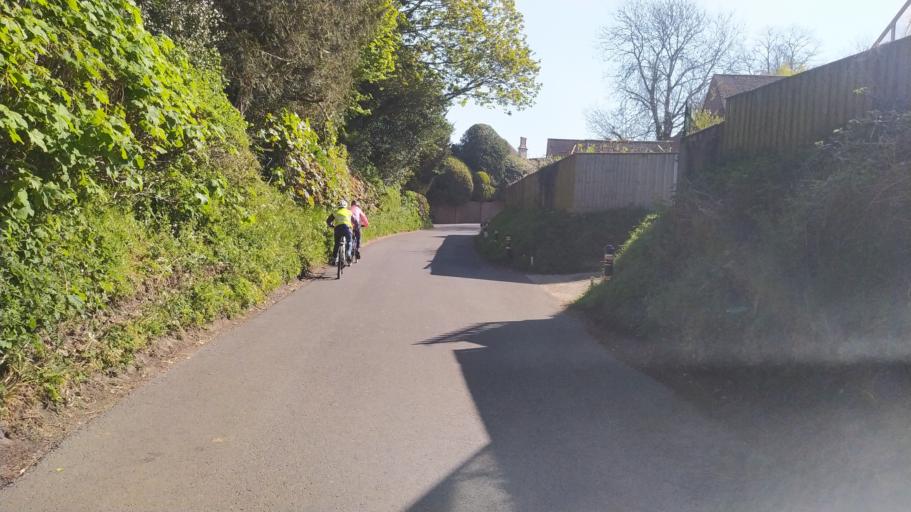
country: GB
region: England
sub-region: Dorset
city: Manston
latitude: 50.9135
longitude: -2.2393
